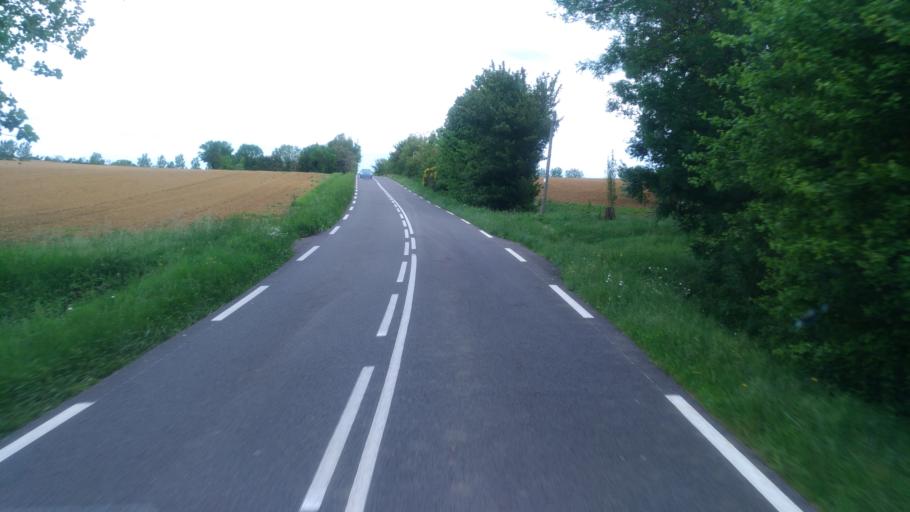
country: FR
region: Midi-Pyrenees
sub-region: Departement de la Haute-Garonne
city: Villefranche-de-Lauragais
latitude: 43.4316
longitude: 1.7723
